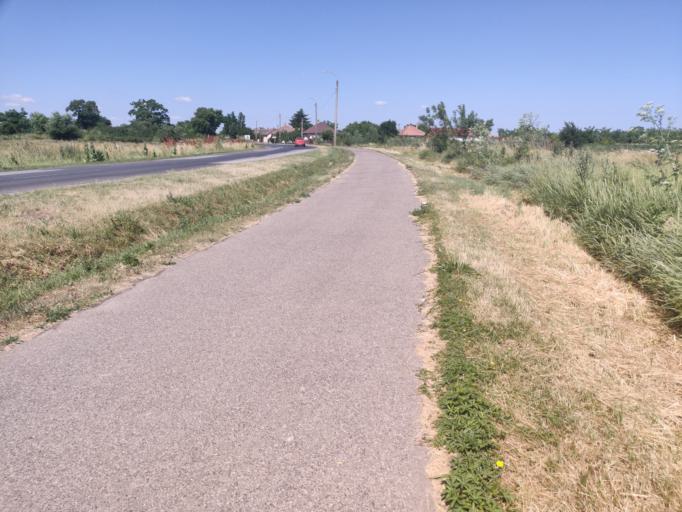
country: HU
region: Hajdu-Bihar
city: Balmazujvaros
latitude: 47.6075
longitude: 21.3696
